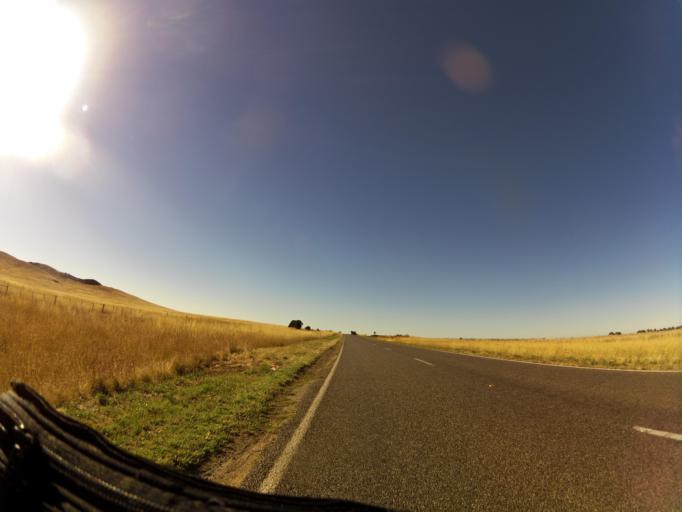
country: AU
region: Victoria
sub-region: Ballarat North
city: Delacombe
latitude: -37.6352
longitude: 143.3443
